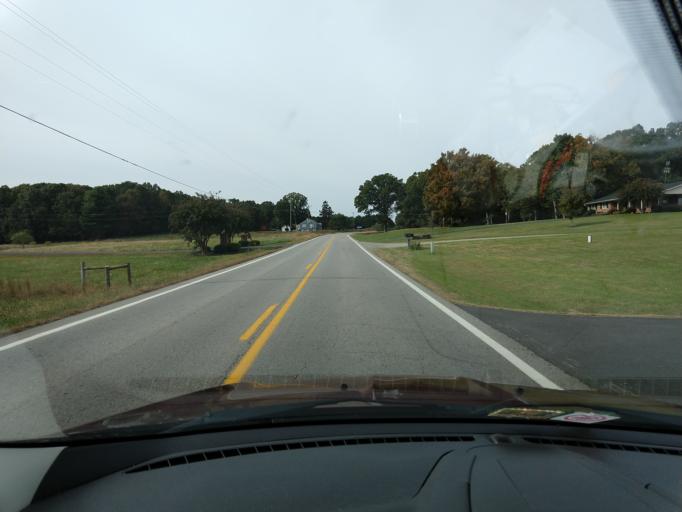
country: US
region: Virginia
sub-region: Pittsylvania County
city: Gretna
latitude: 36.9455
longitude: -79.4627
